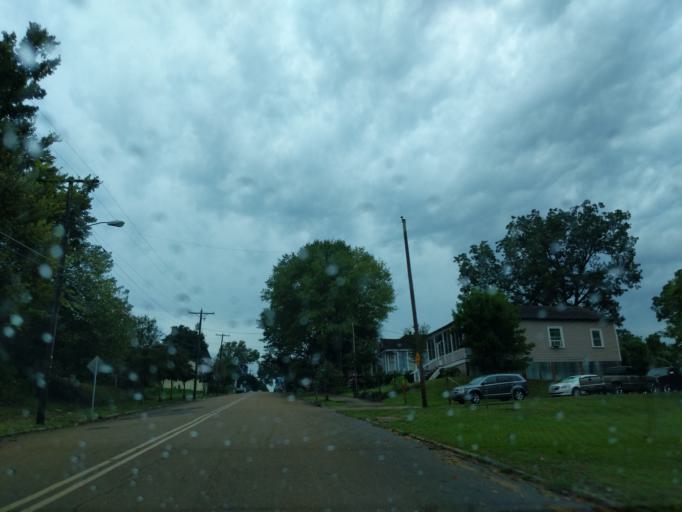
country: US
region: Mississippi
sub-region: Warren County
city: Vicksburg
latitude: 32.3564
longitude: -90.8775
